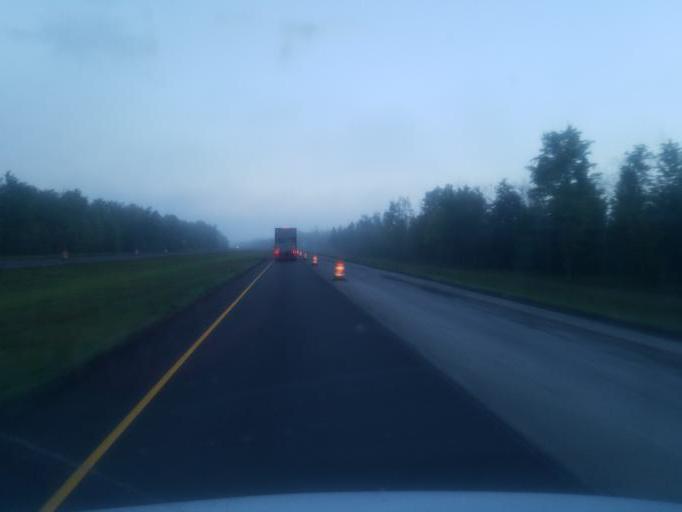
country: US
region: Ohio
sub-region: Ashtabula County
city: Jefferson
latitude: 41.7385
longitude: -80.7079
